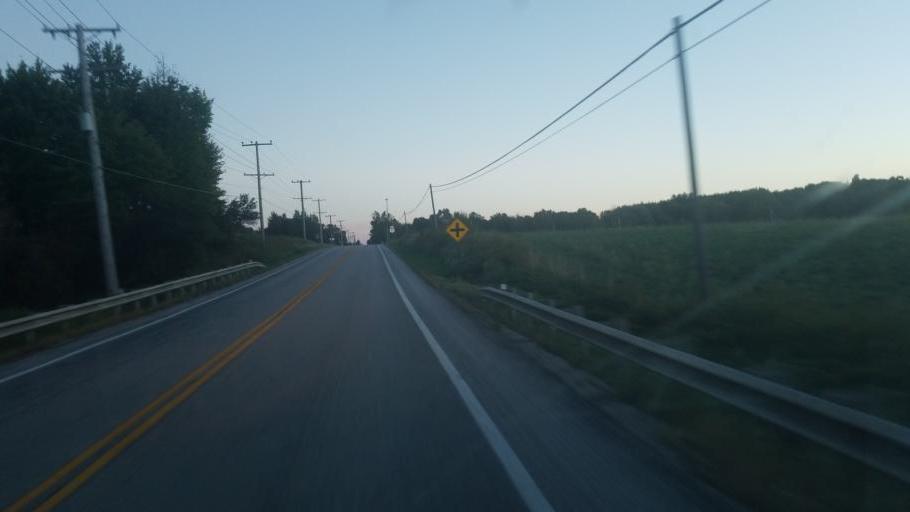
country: US
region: Ohio
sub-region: Ashtabula County
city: Andover
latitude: 41.7676
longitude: -80.5717
